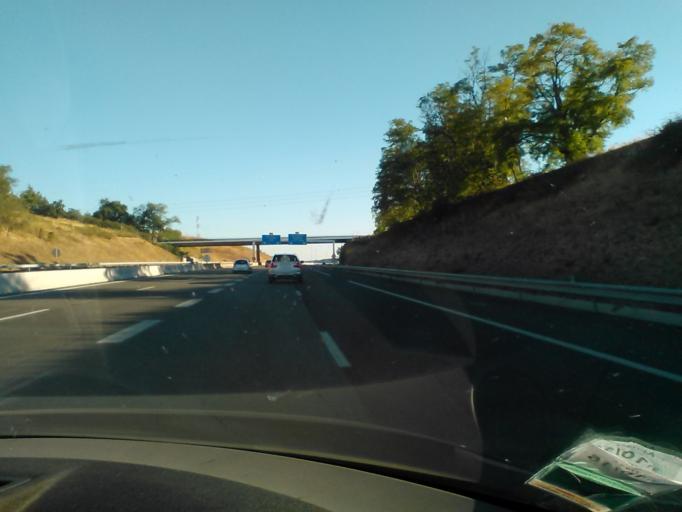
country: FR
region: Rhone-Alpes
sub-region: Departement du Rhone
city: Saint-Laurent-de-Mure
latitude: 45.6779
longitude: 5.0529
